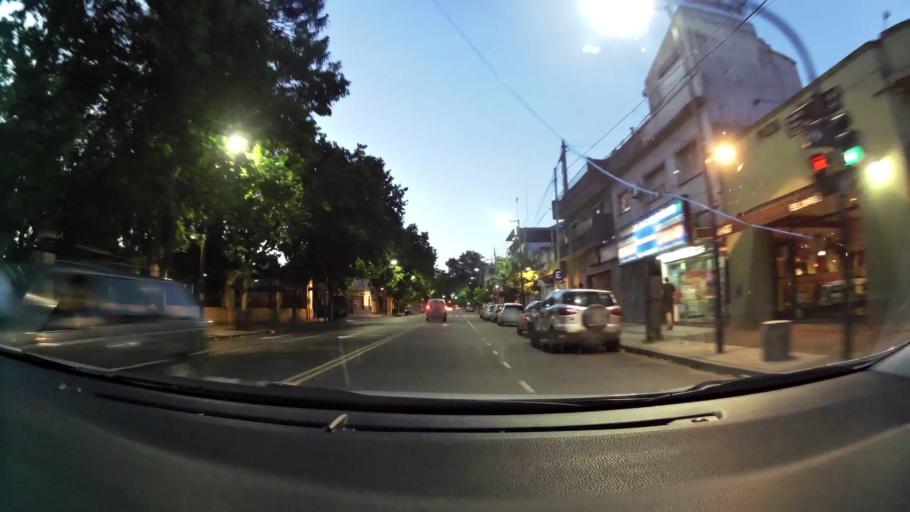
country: AR
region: Buenos Aires F.D.
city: Villa Lugano
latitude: -34.6437
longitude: -58.4540
